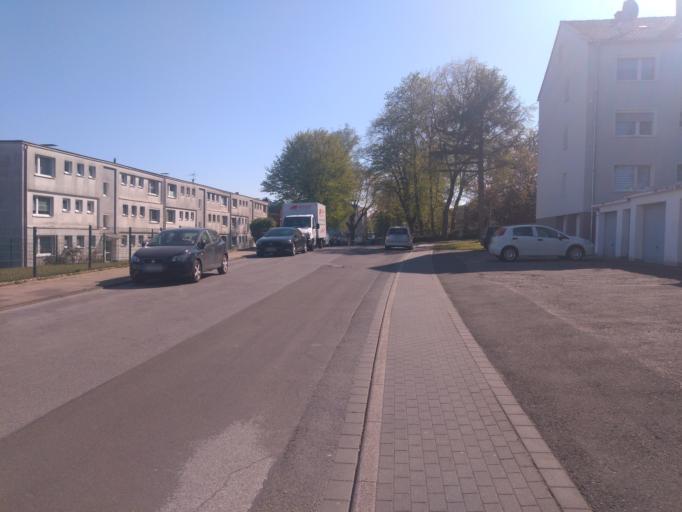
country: DE
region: North Rhine-Westphalia
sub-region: Regierungsbezirk Dusseldorf
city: Velbert
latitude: 51.3055
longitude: 7.1042
